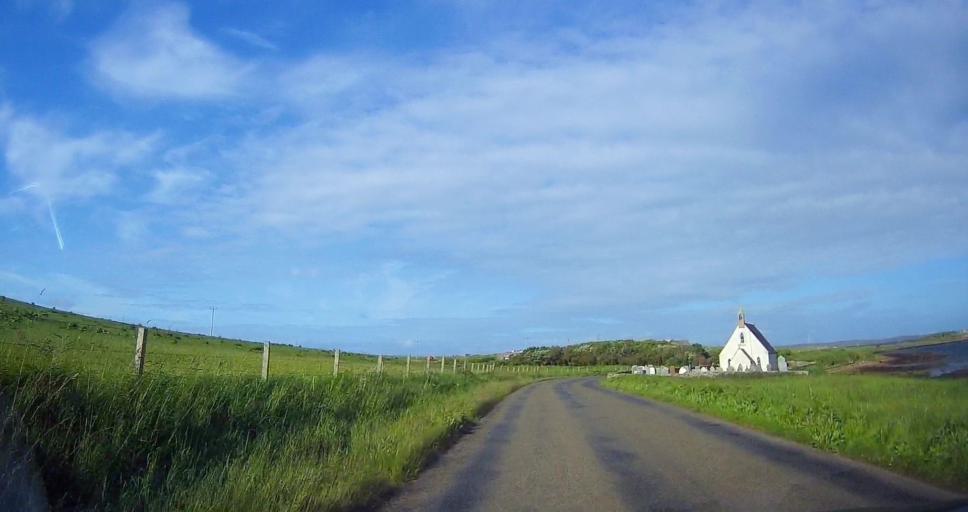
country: GB
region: Scotland
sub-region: Orkney Islands
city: Stromness
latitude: 58.8051
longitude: -3.2193
